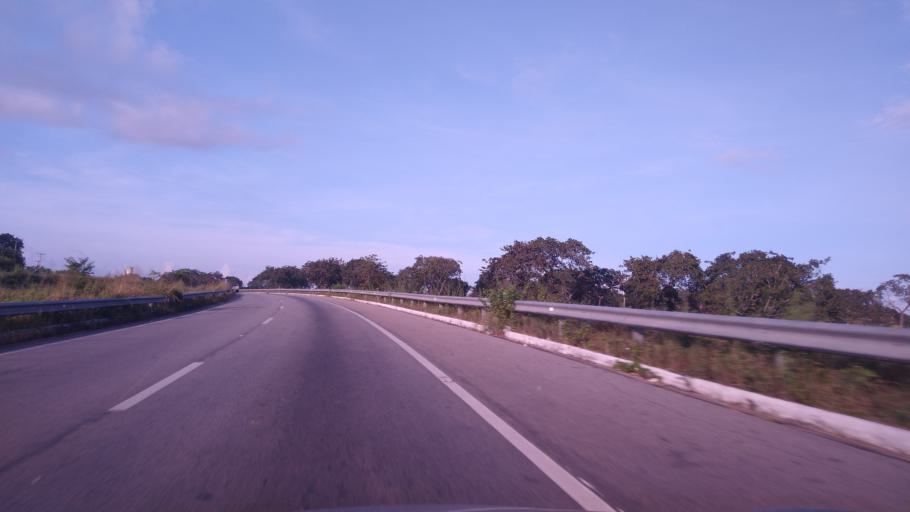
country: BR
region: Ceara
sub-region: Pacajus
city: Pacajus
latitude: -4.1680
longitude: -38.4926
